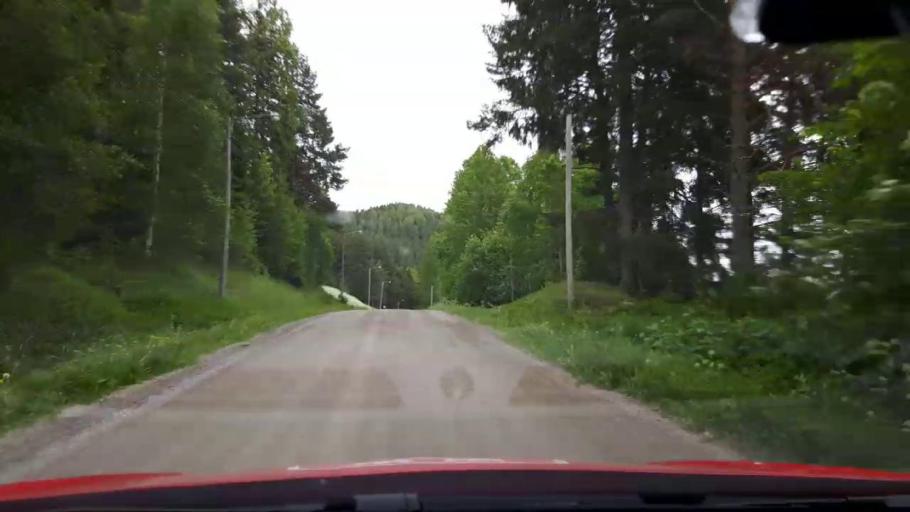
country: SE
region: Jaemtland
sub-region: Ragunda Kommun
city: Hammarstrand
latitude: 63.1755
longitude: 16.1972
